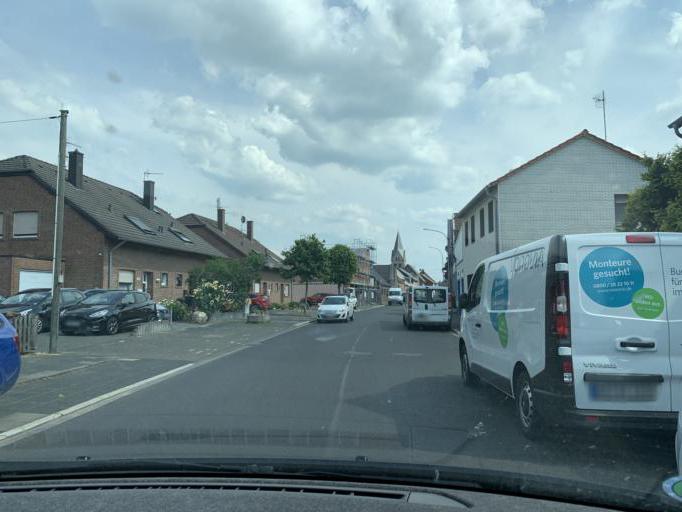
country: DE
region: North Rhine-Westphalia
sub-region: Regierungsbezirk Koln
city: Bergheim
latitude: 50.9651
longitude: 6.6053
